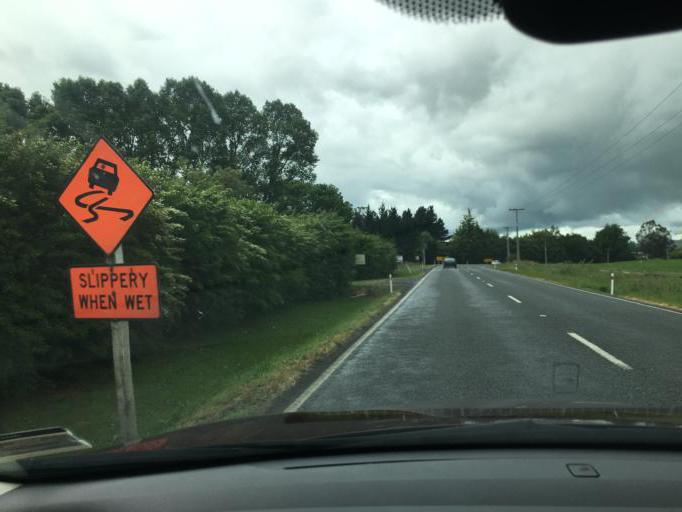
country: NZ
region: Waikato
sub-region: Waipa District
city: Cambridge
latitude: -37.9033
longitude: 175.4517
